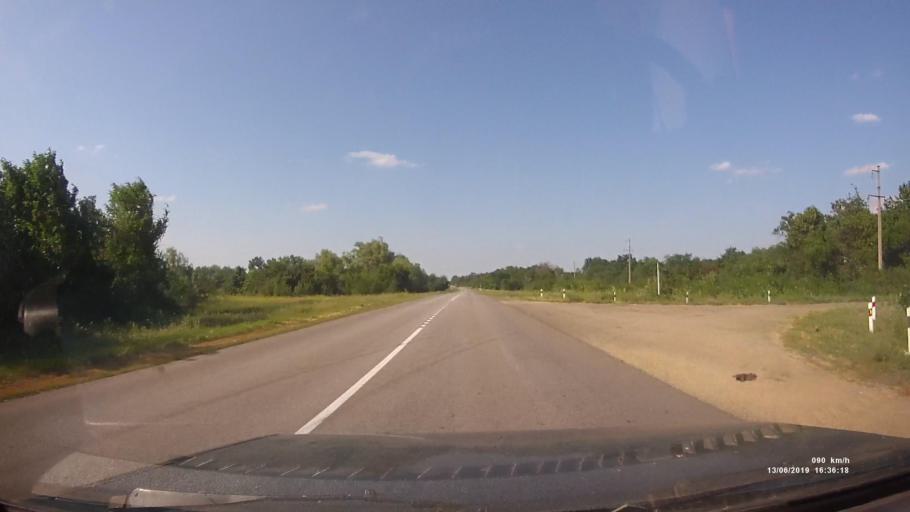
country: RU
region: Rostov
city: Kazanskaya
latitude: 49.8934
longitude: 41.3050
